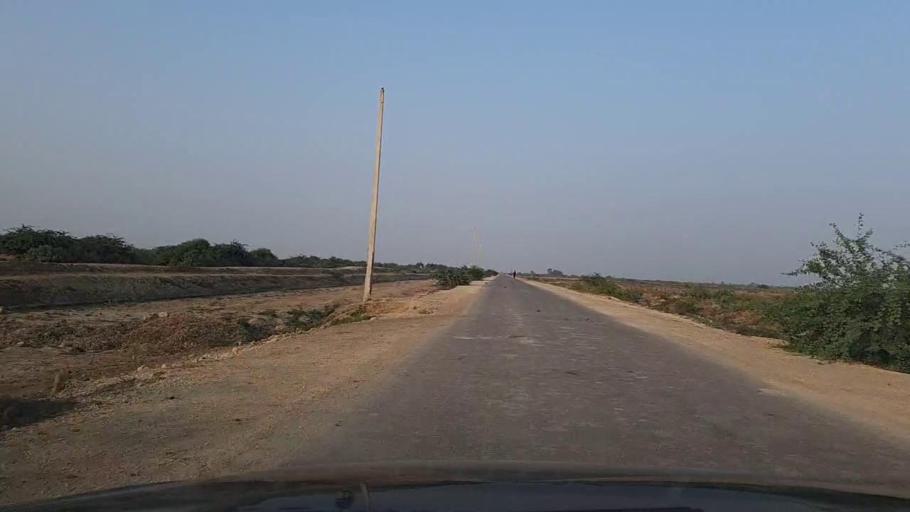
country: PK
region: Sindh
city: Mirpur Sakro
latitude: 24.4710
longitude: 67.8003
